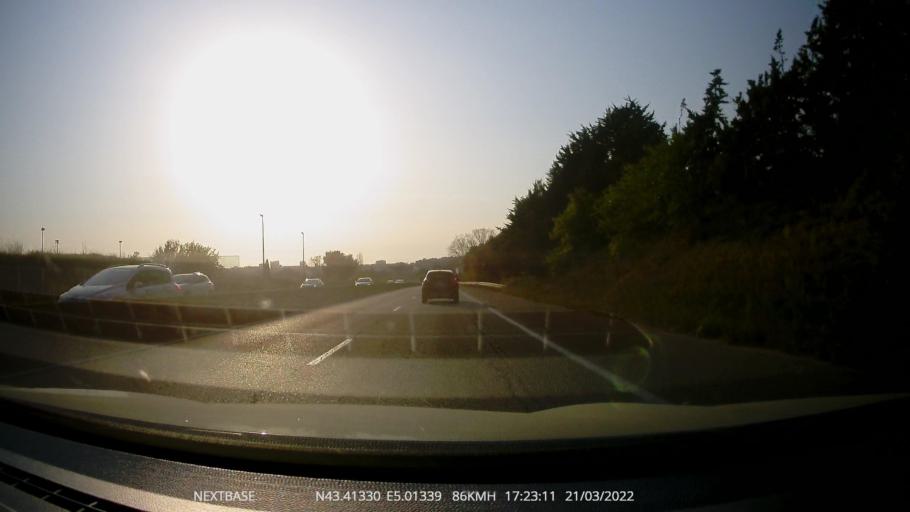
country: FR
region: Provence-Alpes-Cote d'Azur
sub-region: Departement des Bouches-du-Rhone
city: Port-de-Bouc
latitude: 43.4133
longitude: 5.0130
